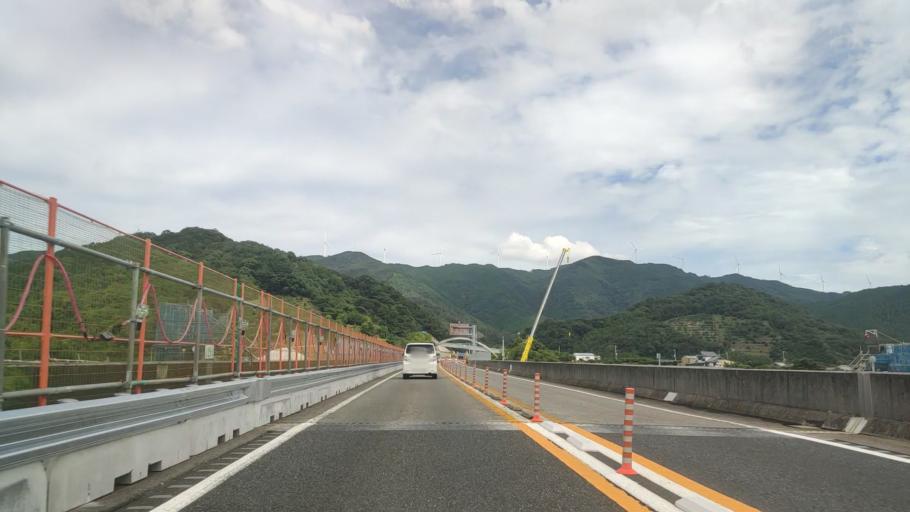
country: JP
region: Wakayama
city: Gobo
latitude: 33.9317
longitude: 135.1940
